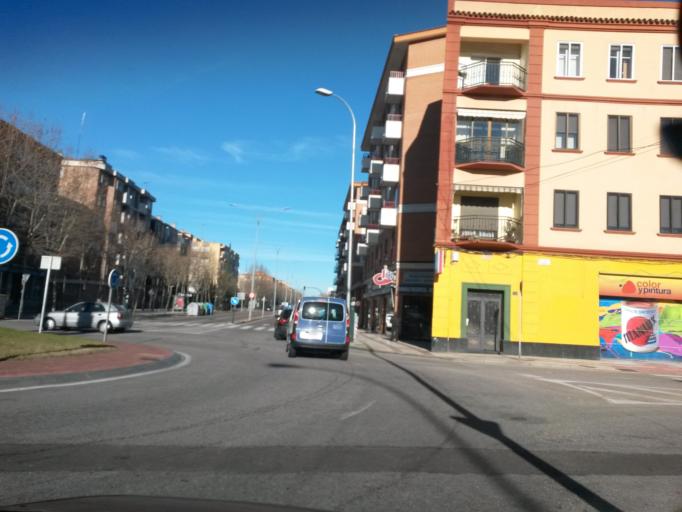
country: ES
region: Castille and Leon
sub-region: Provincia de Salamanca
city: Salamanca
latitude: 40.9734
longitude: -5.6464
